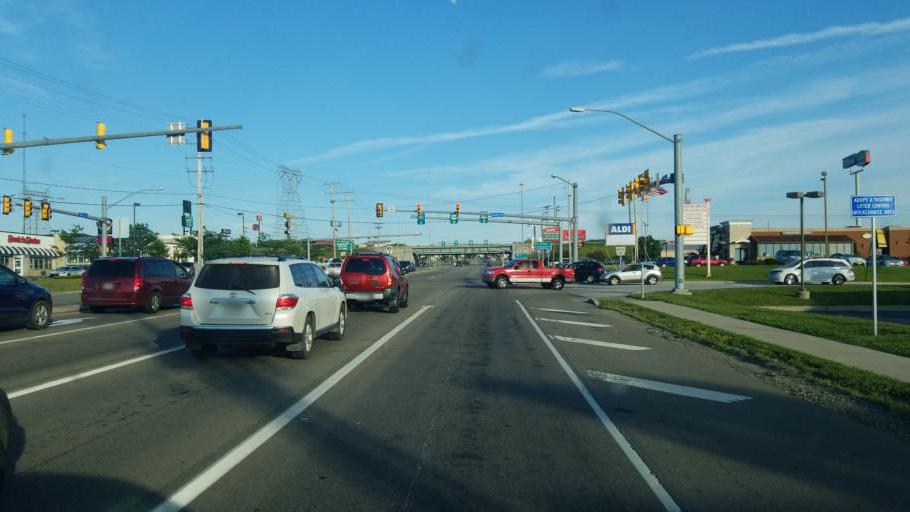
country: US
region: Pennsylvania
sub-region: Erie County
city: Erie
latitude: 42.0518
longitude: -80.0842
